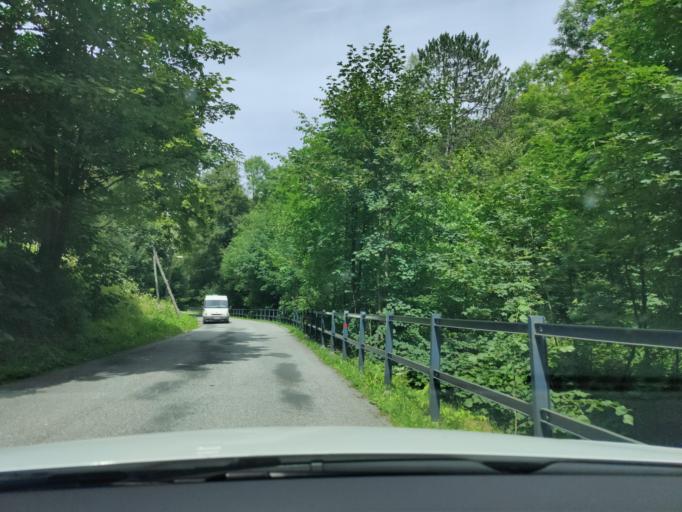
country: CZ
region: Olomoucky
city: Zlate Hory
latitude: 50.2244
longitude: 17.3451
